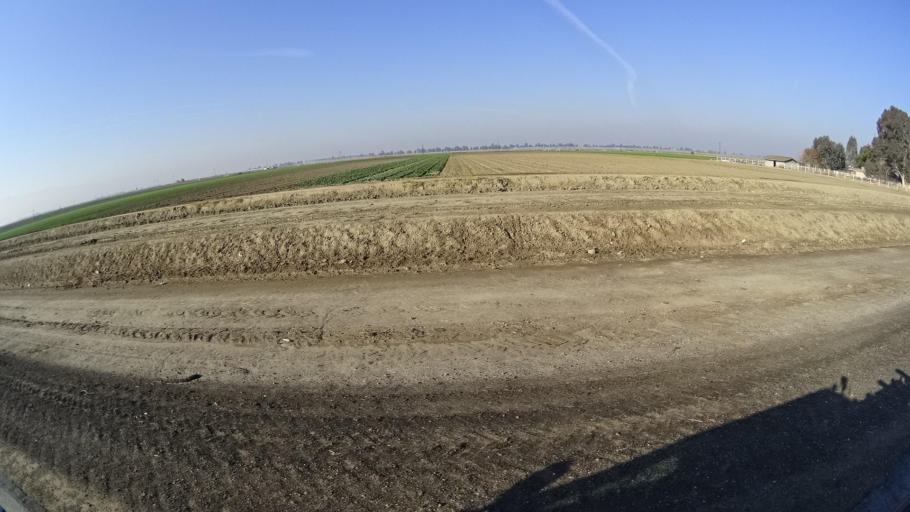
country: US
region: California
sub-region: Kern County
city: Weedpatch
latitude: 35.1849
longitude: -118.9677
